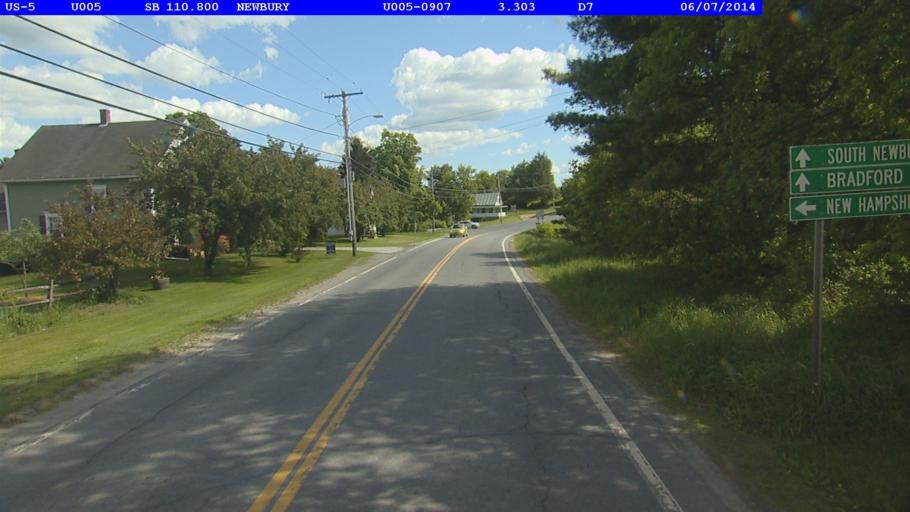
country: US
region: New Hampshire
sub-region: Grafton County
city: North Haverhill
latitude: 44.0727
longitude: -72.0573
